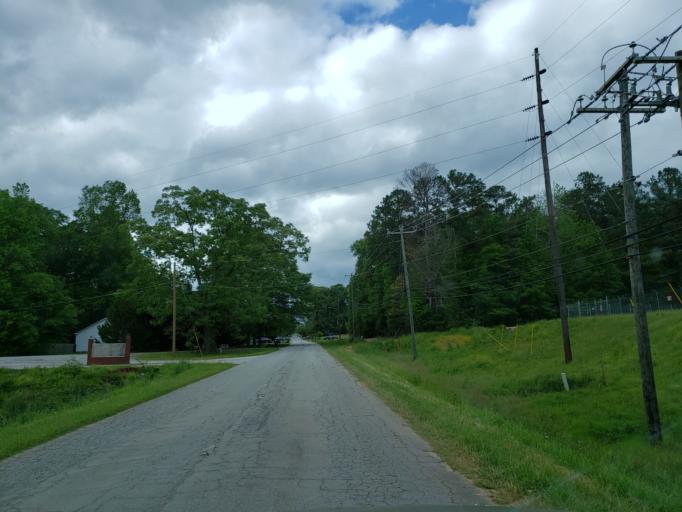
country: US
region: Georgia
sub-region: Haralson County
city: Tallapoosa
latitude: 33.7386
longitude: -85.2911
